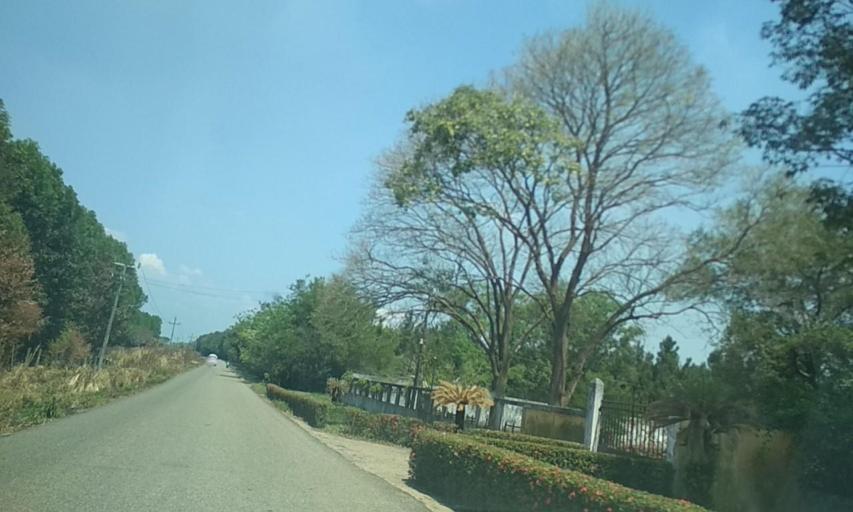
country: MX
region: Tabasco
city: Huimanguillo
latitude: 17.7999
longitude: -93.4703
